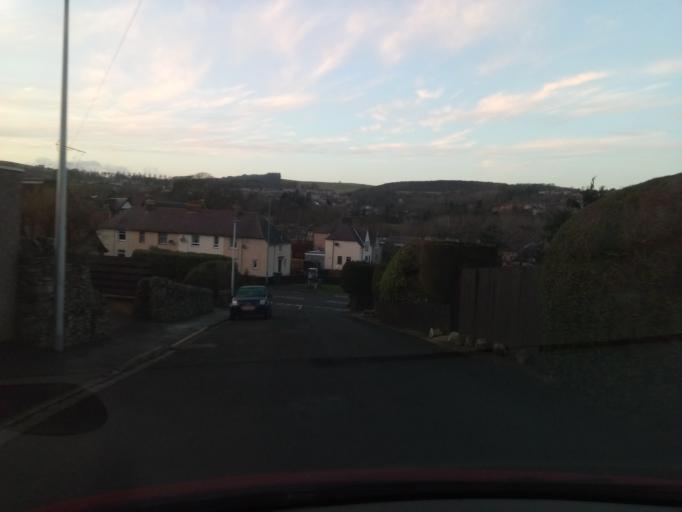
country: GB
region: Scotland
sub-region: The Scottish Borders
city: Hawick
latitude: 55.4279
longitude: -2.7736
